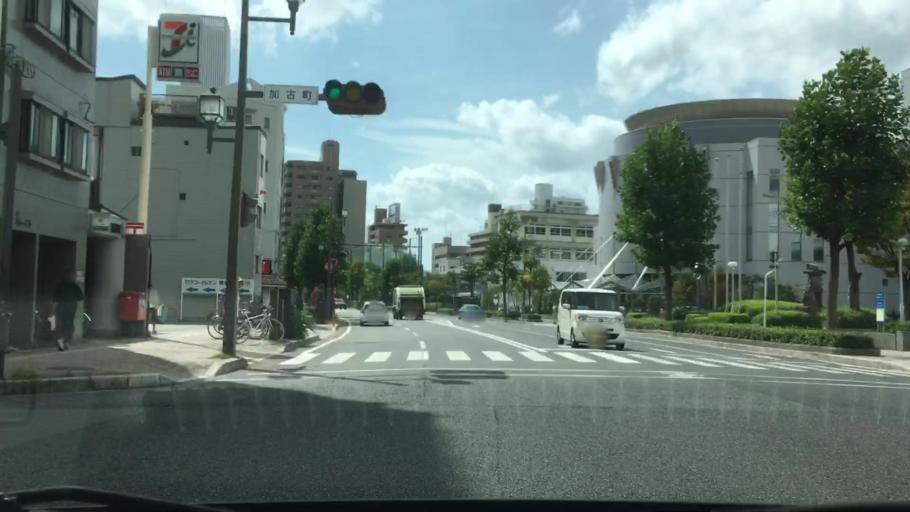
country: JP
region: Hiroshima
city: Hiroshima-shi
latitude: 34.3880
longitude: 132.4491
